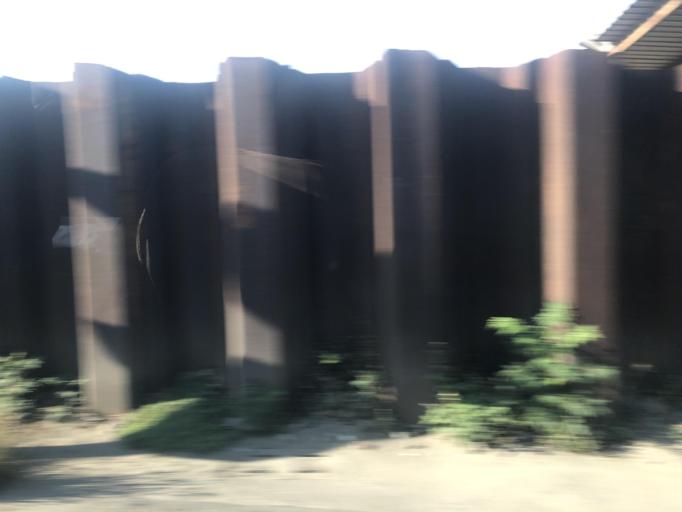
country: TW
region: Taiwan
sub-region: Tainan
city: Tainan
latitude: 23.0299
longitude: 120.2000
